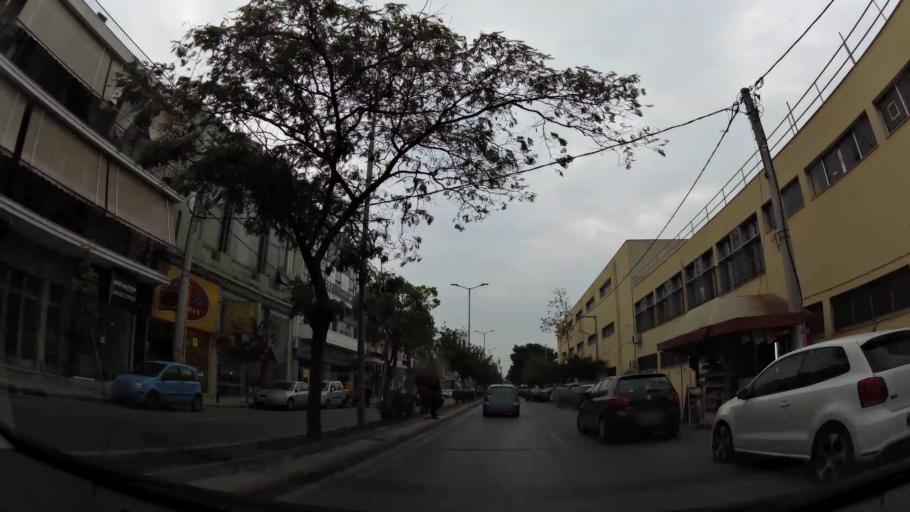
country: GR
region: Attica
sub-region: Nomarchia Athinas
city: Aigaleo
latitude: 37.9941
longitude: 23.6795
